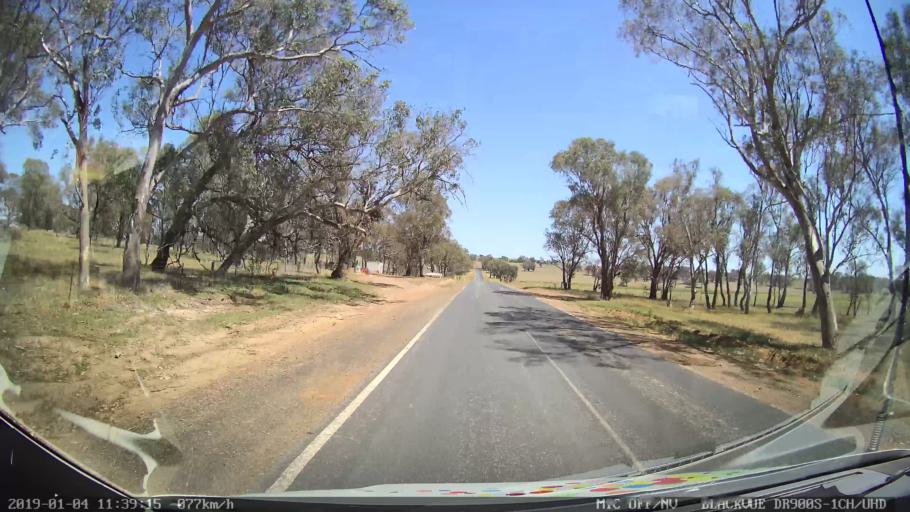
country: AU
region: New South Wales
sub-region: Cabonne
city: Molong
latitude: -33.0150
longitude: 148.7972
